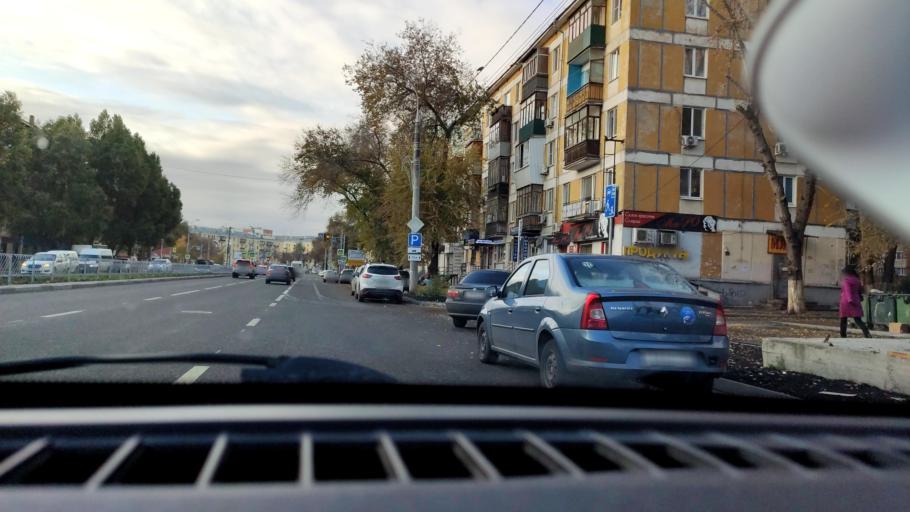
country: RU
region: Samara
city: Samara
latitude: 53.2039
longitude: 50.2289
